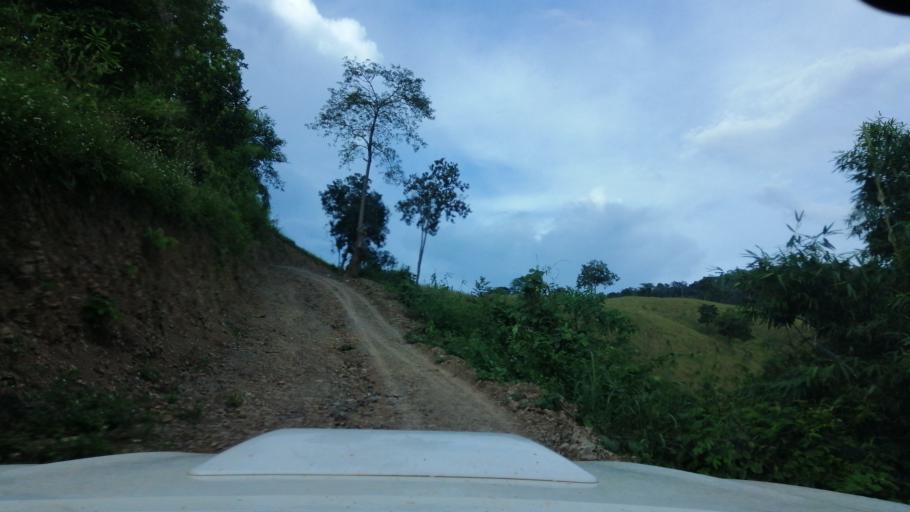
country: TH
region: Nan
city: Chaloem Phra Kiat
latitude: 19.7562
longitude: 101.1091
